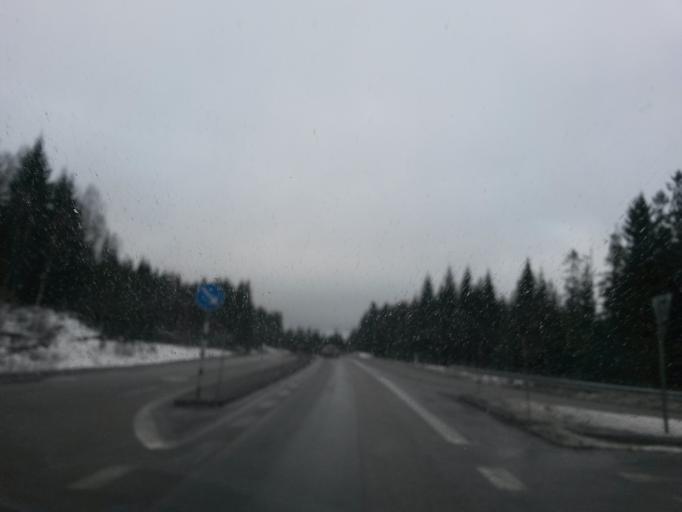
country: SE
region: Vaestra Goetaland
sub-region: Boras Kommun
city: Boras
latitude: 57.6536
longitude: 12.9188
